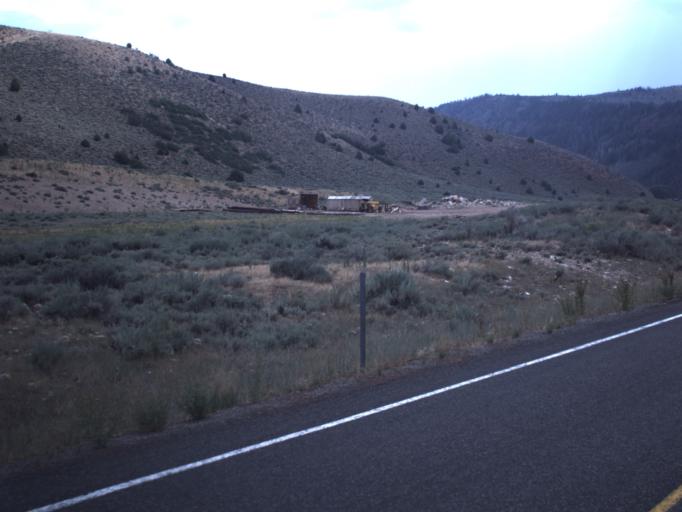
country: US
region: Utah
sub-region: Summit County
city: Francis
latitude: 40.4593
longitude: -110.8923
